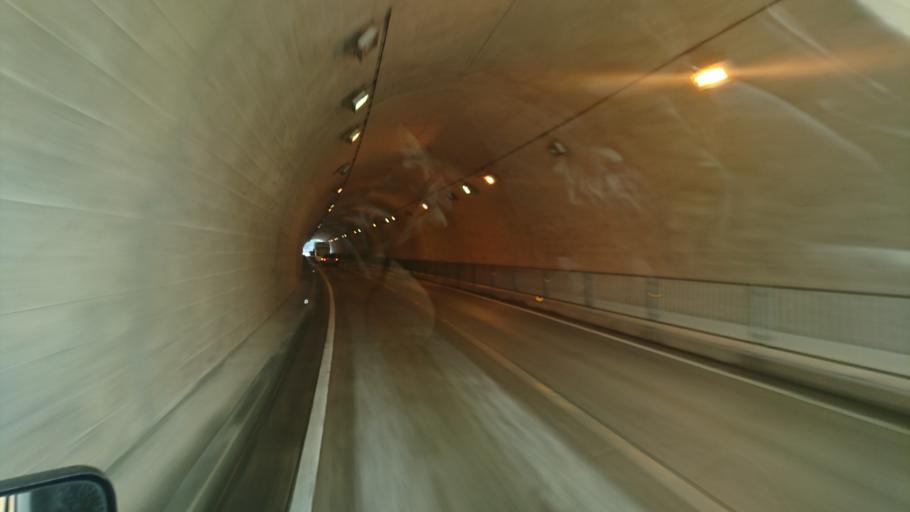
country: JP
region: Tottori
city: Tottori
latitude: 35.6056
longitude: 134.4704
